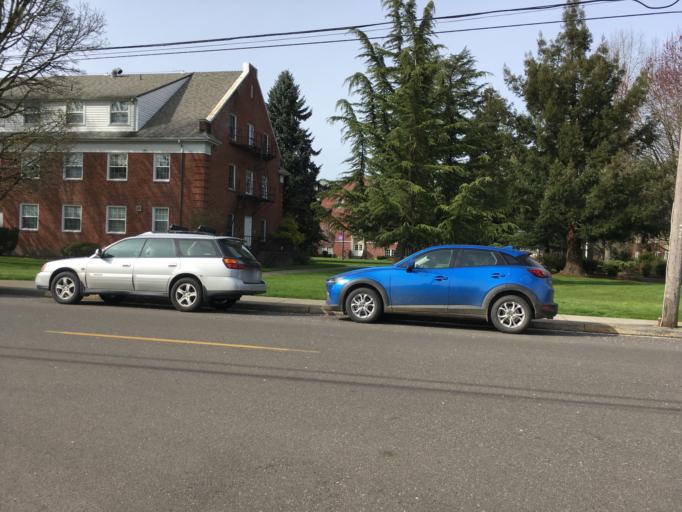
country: US
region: Oregon
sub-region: Yamhill County
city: McMinnville
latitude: 45.2002
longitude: -123.2002
